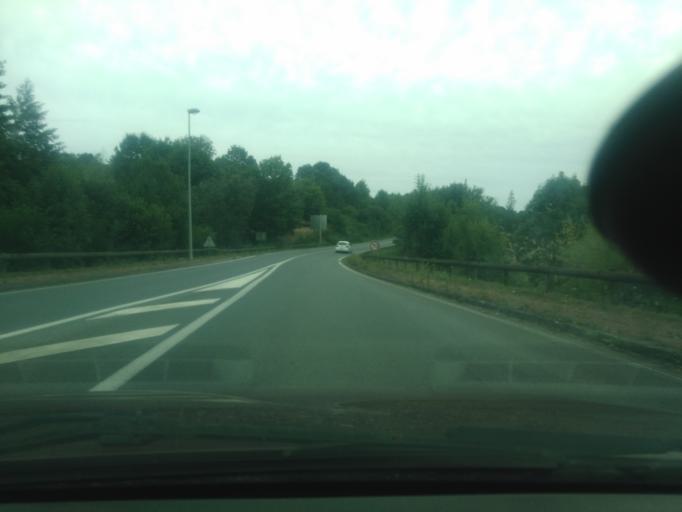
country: FR
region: Pays de la Loire
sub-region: Departement de la Vendee
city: Antigny
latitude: 46.6659
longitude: -0.7921
